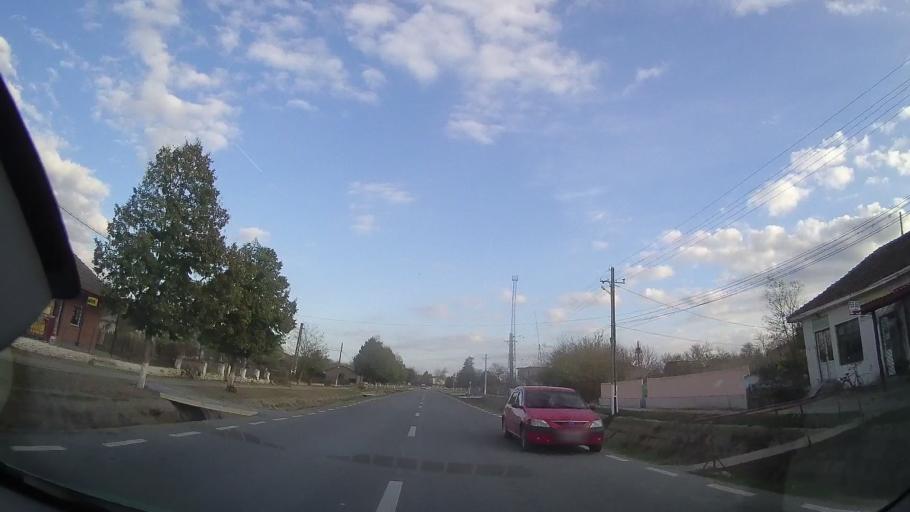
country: RO
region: Constanta
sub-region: Comuna Independenta
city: Independenta
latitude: 43.9526
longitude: 28.0803
